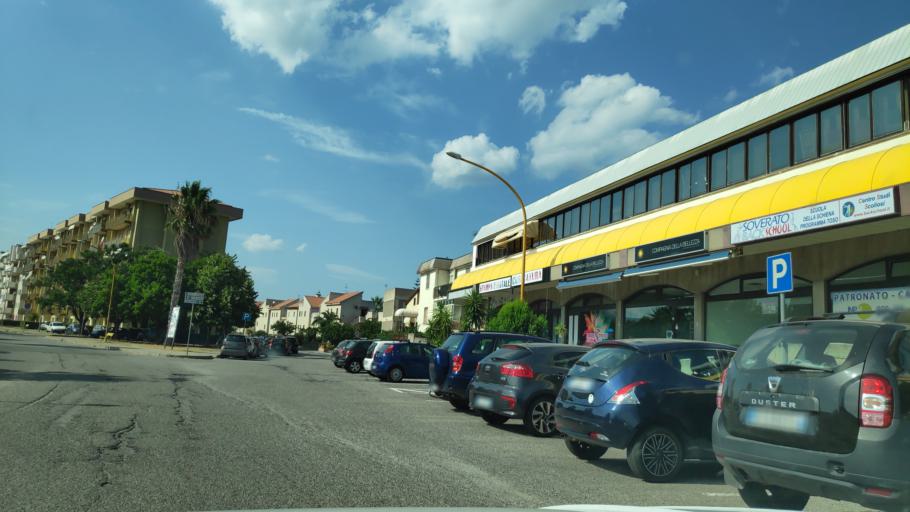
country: IT
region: Calabria
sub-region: Provincia di Catanzaro
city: Soverato Marina
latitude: 38.6809
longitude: 16.5553
